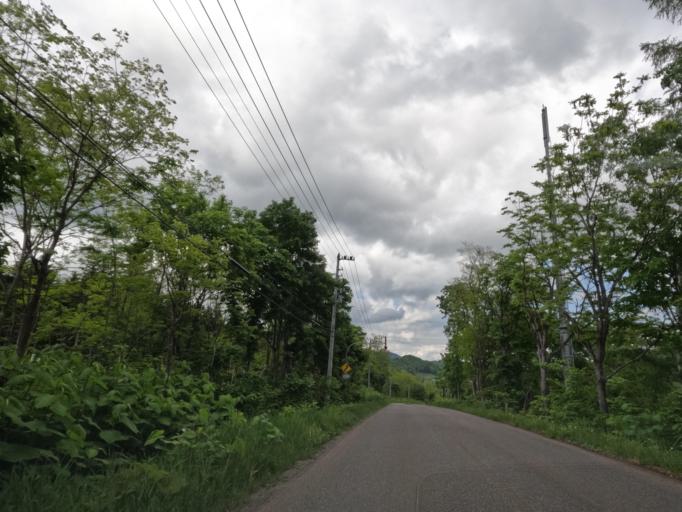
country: JP
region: Hokkaido
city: Takikawa
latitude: 43.5717
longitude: 141.7085
